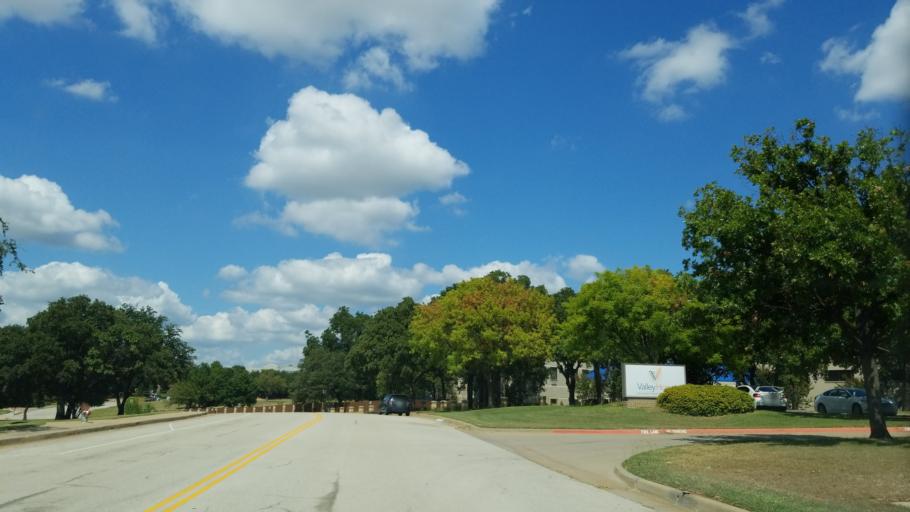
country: US
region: Texas
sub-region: Tarrant County
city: Grapevine
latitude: 32.9135
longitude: -97.1008
